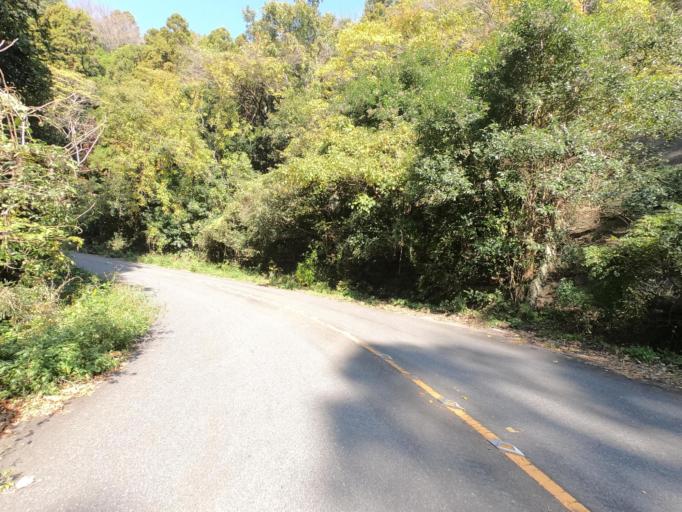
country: JP
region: Ibaraki
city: Tsukuba
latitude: 36.1684
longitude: 140.1757
